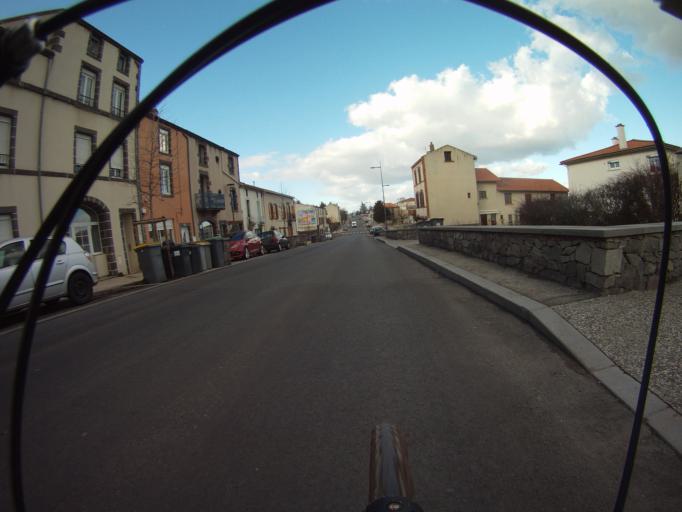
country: FR
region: Auvergne
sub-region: Departement du Puy-de-Dome
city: Perignat-les-Sarlieve
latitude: 45.7370
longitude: 3.1411
